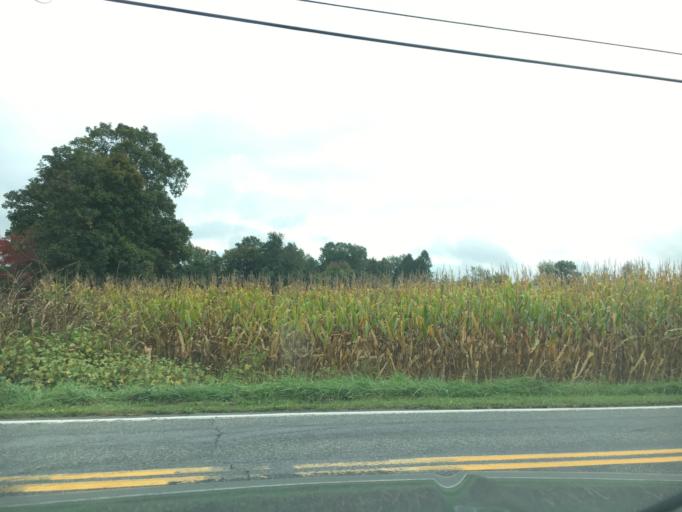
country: US
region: Pennsylvania
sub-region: Berks County
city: Topton
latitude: 40.4551
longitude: -75.7475
